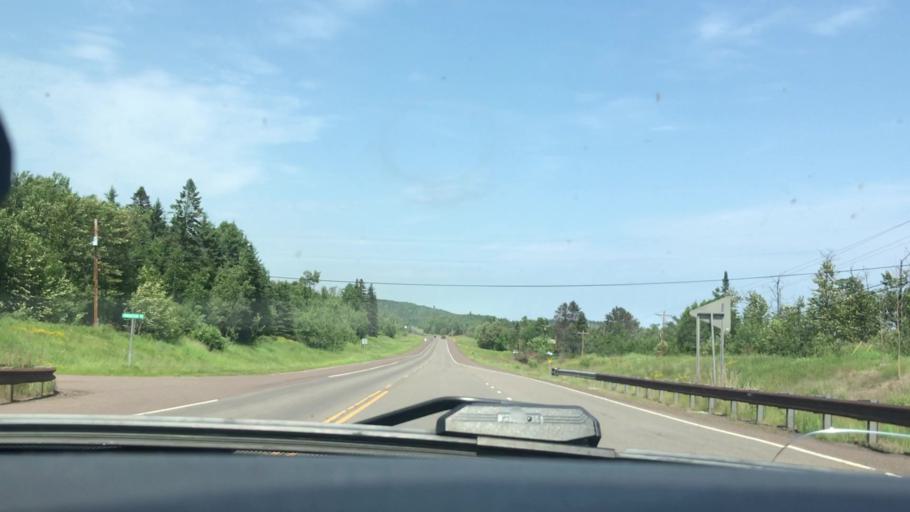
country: US
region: Minnesota
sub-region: Lake County
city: Silver Bay
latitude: 47.3228
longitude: -91.2158
